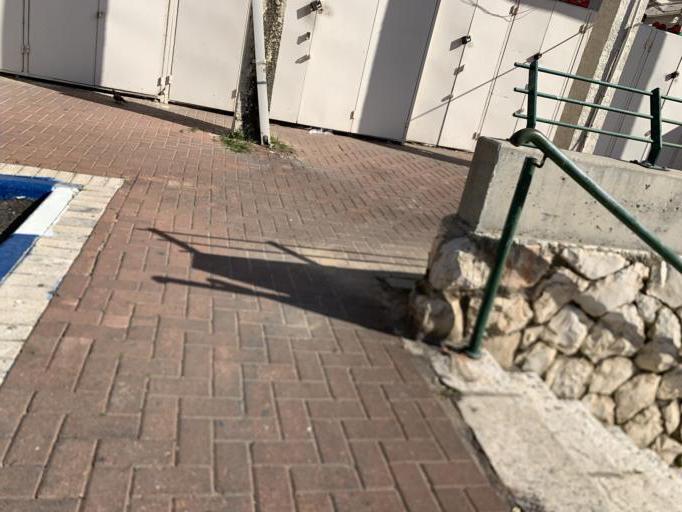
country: IL
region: Tel Aviv
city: Ramat Gan
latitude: 32.0887
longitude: 34.8034
